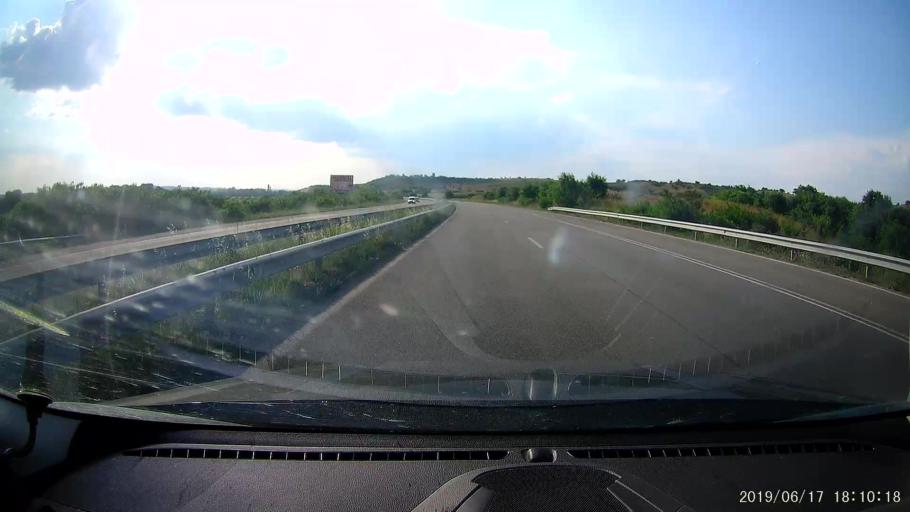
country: BG
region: Khaskovo
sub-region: Obshtina Lyubimets
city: Lyubimets
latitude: 41.8729
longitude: 26.0801
